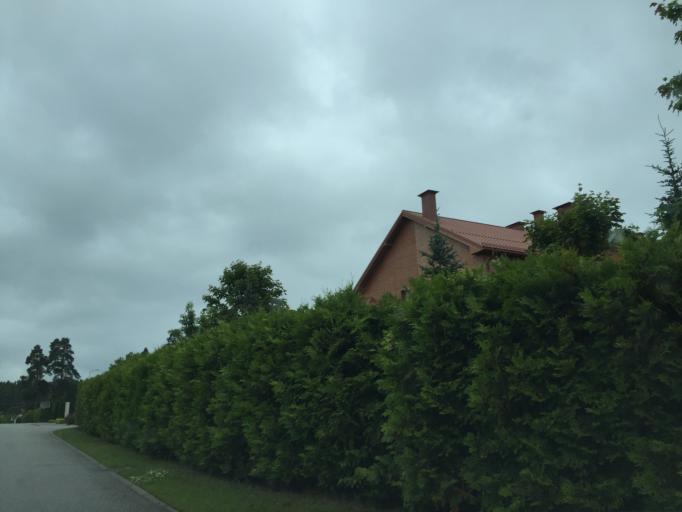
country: LV
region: Riga
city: Jaunciems
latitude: 57.0177
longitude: 24.2162
